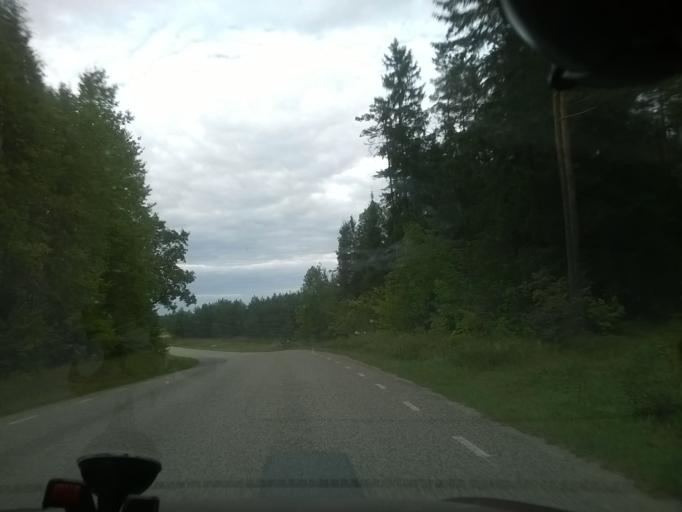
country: EE
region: Vorumaa
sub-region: Voru linn
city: Voru
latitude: 57.7421
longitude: 26.9545
